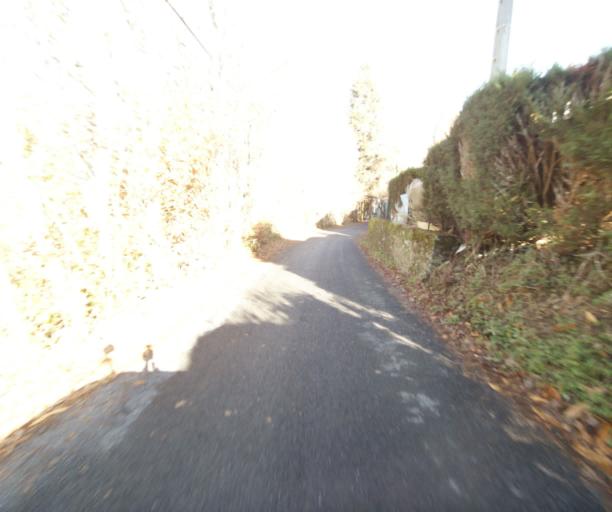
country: FR
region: Limousin
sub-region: Departement de la Correze
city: Laguenne
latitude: 45.2392
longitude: 1.7530
